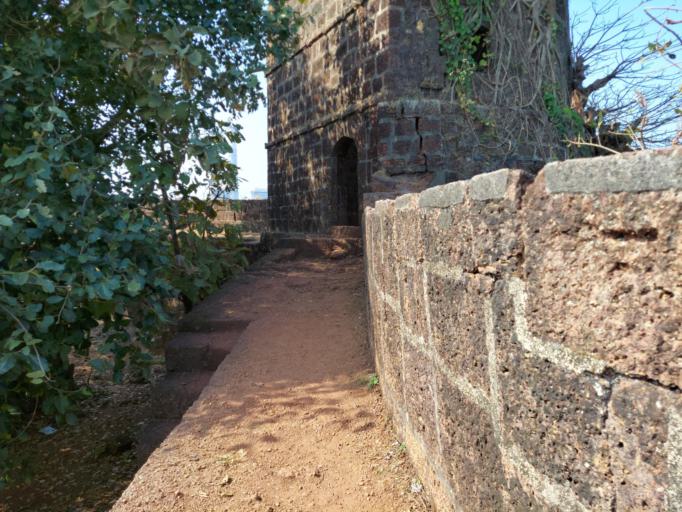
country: IN
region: Maharashtra
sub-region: Ratnagiri
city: Guhagar
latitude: 17.3017
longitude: 73.2211
